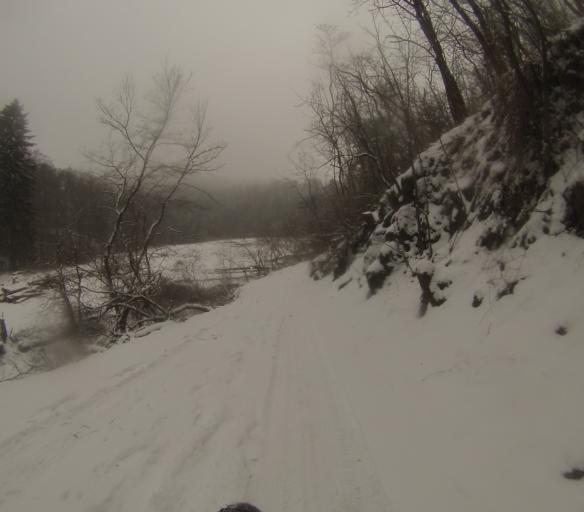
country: CZ
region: South Moravian
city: Zelesice
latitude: 49.1291
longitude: 16.5550
